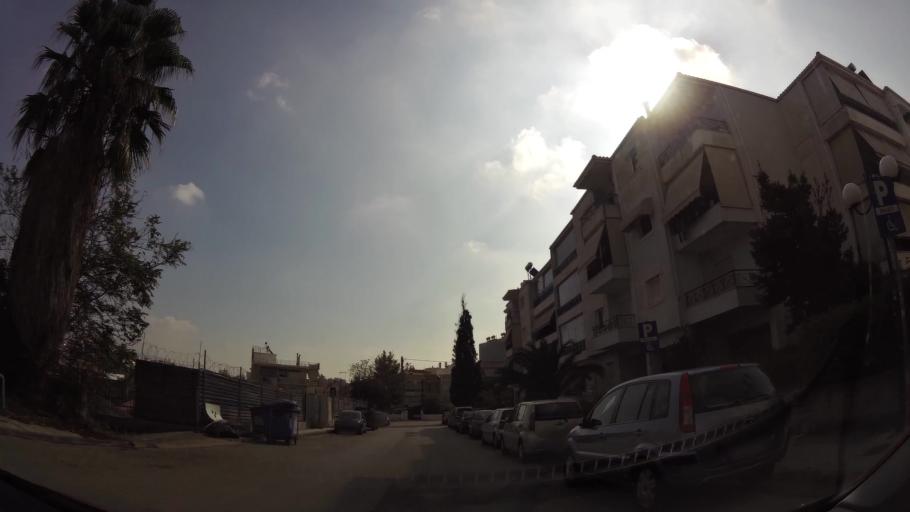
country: GR
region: Attica
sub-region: Nomarchia Dytikis Attikis
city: Zefyri
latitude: 38.0630
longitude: 23.7286
